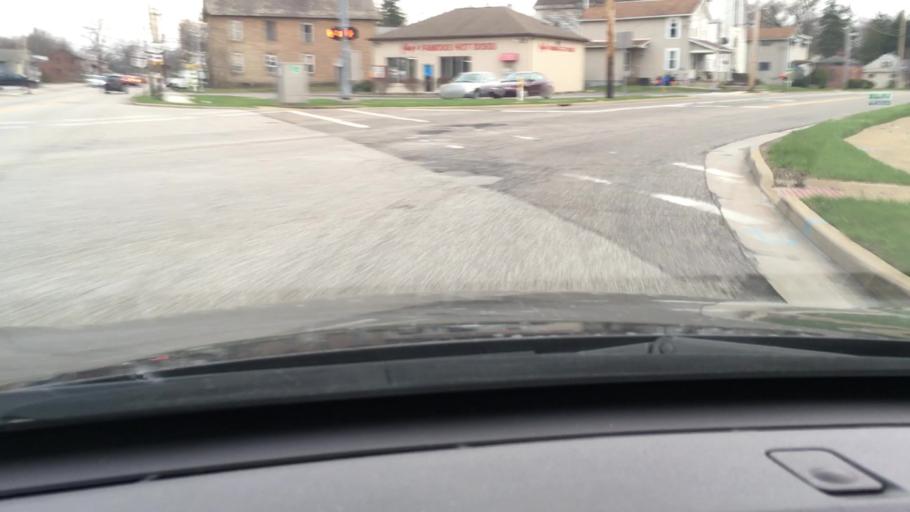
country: US
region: Ohio
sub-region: Columbiana County
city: Columbiana
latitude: 40.9482
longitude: -80.6586
